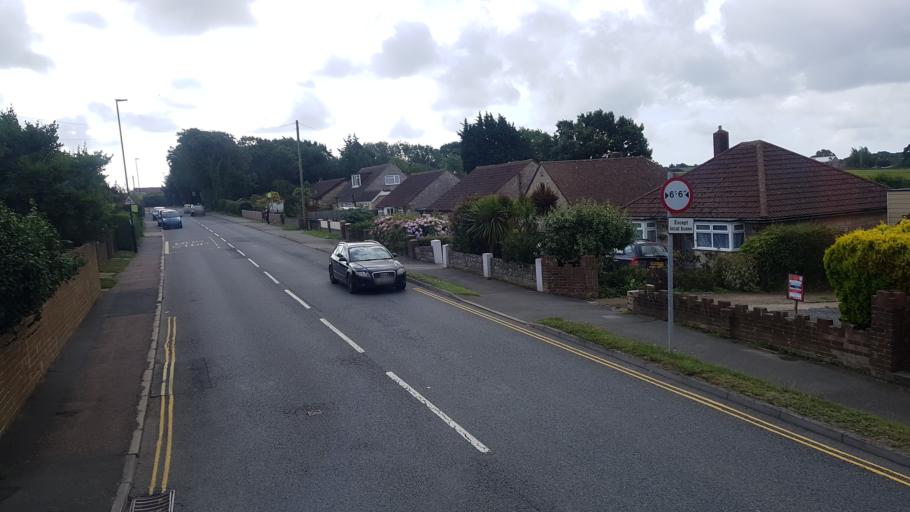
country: GB
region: England
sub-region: Isle of Wight
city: Ryde
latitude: 50.7159
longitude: -1.1505
